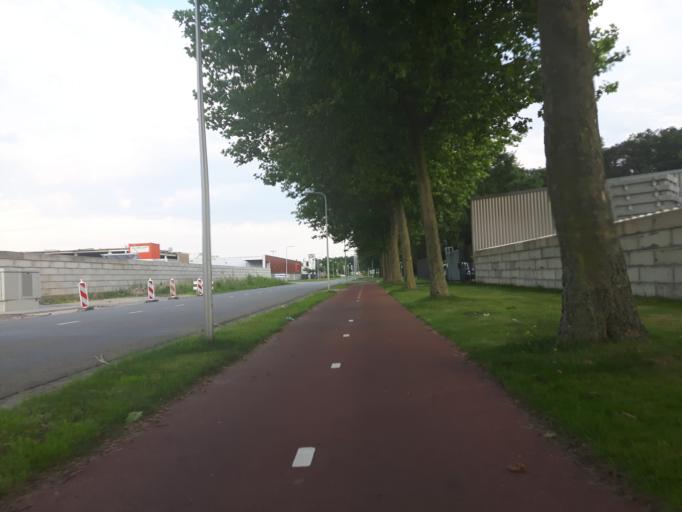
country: NL
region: Overijssel
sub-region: Gemeente Enschede
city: Enschede
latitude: 52.2217
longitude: 6.8481
